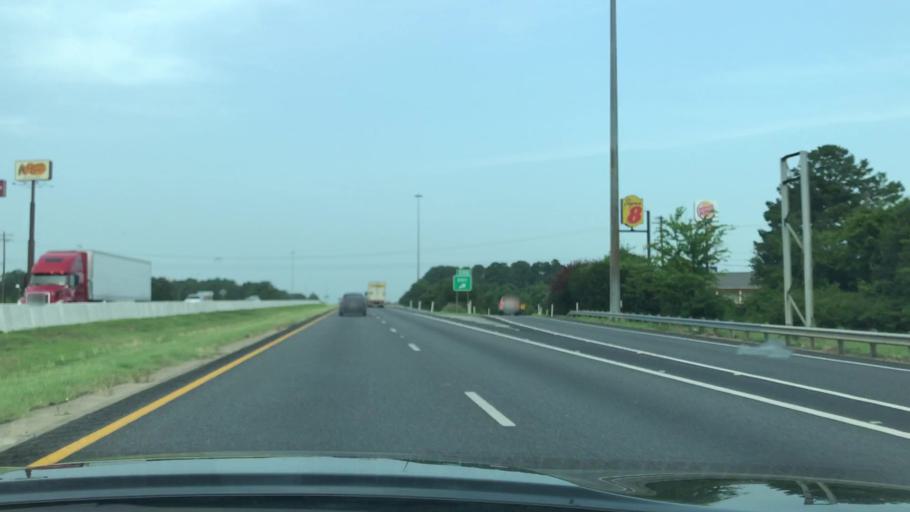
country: US
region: Texas
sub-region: Gregg County
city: Longview
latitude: 32.4514
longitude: -94.7055
